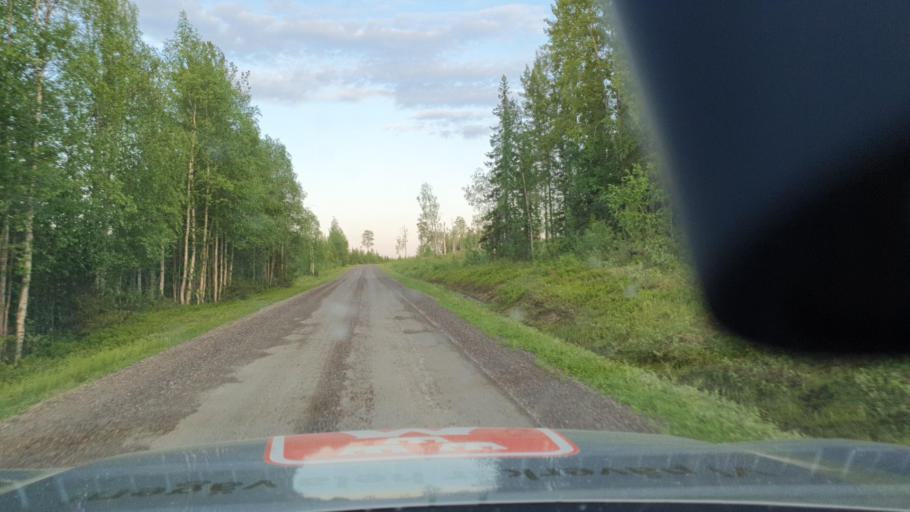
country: SE
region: Norrbotten
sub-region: Bodens Kommun
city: Boden
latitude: 66.4759
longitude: 21.6210
